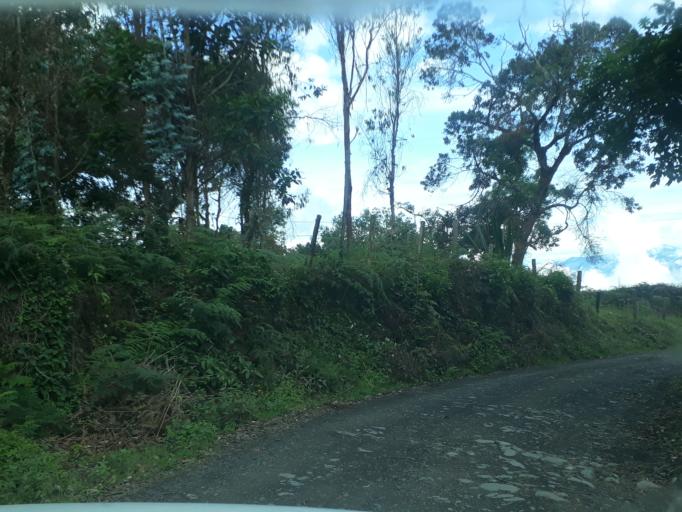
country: CO
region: Cundinamarca
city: Carmen de Carupa
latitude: 5.3468
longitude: -74.0613
